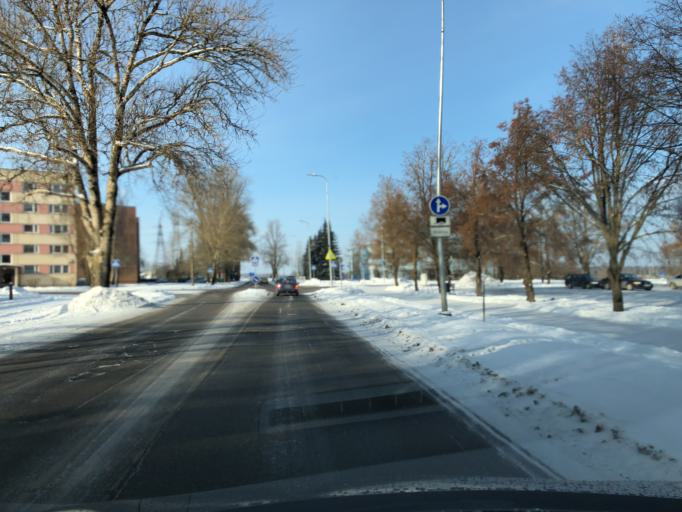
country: EE
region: Tartu
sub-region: Tartu linn
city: Tartu
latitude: 58.3779
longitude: 26.6851
